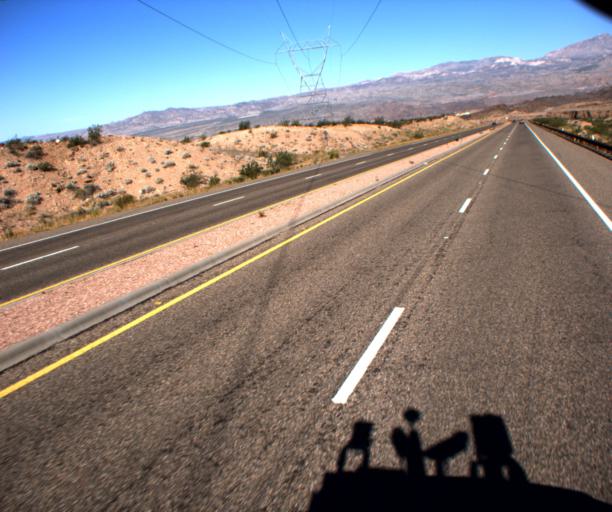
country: US
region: Nevada
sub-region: Clark County
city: Laughlin
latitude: 35.1894
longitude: -114.5118
